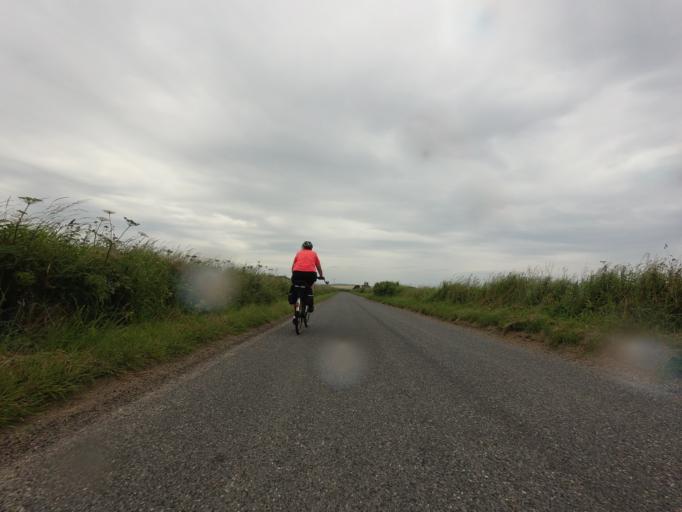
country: GB
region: Scotland
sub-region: Aberdeenshire
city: Portsoy
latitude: 57.6730
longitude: -2.6381
